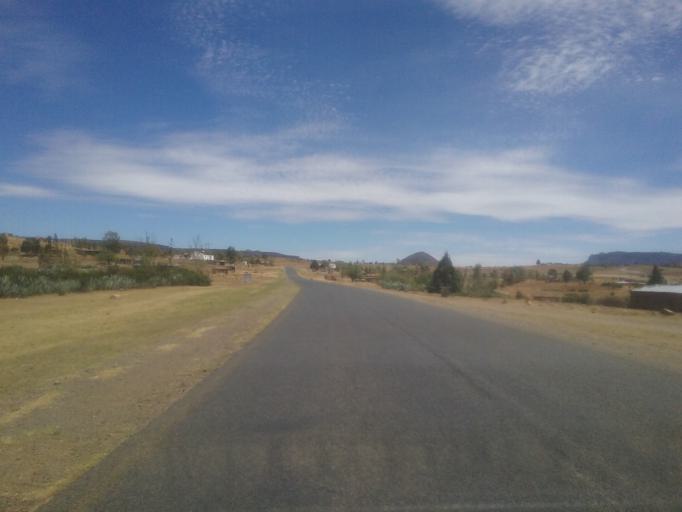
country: LS
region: Mafeteng
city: Mafeteng
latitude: -29.9894
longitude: 27.3324
